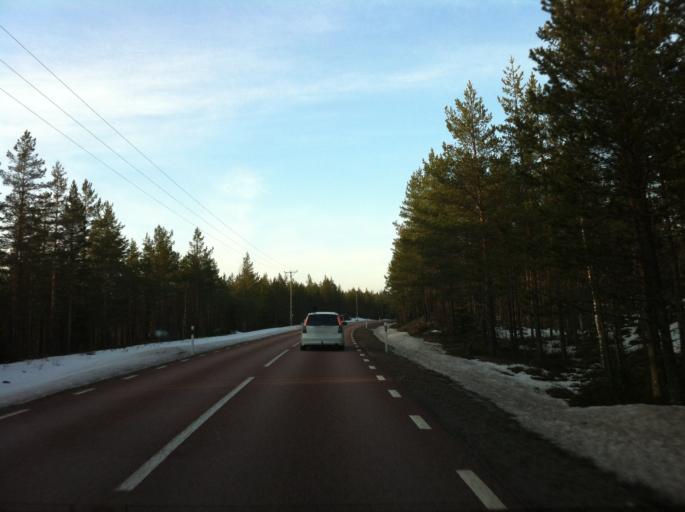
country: SE
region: Vaermland
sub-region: Filipstads Kommun
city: Lesjofors
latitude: 60.1801
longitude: 14.1964
